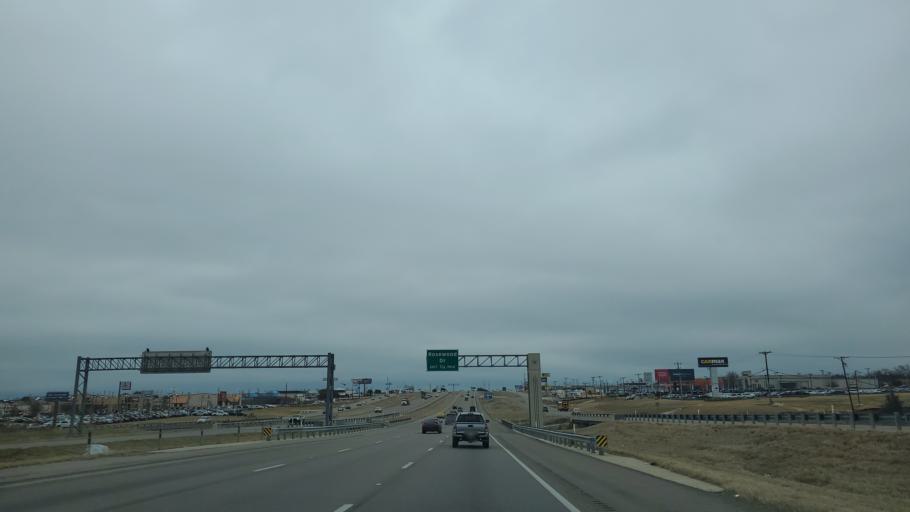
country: US
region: Texas
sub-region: Bell County
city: Killeen
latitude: 31.0851
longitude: -97.7084
